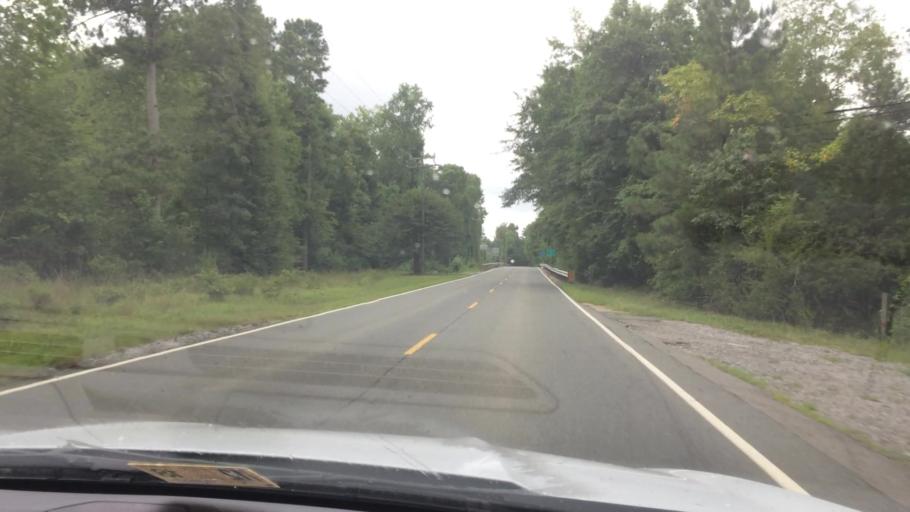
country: US
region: Virginia
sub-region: Charles City County
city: Charles City
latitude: 37.4304
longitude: -77.0380
